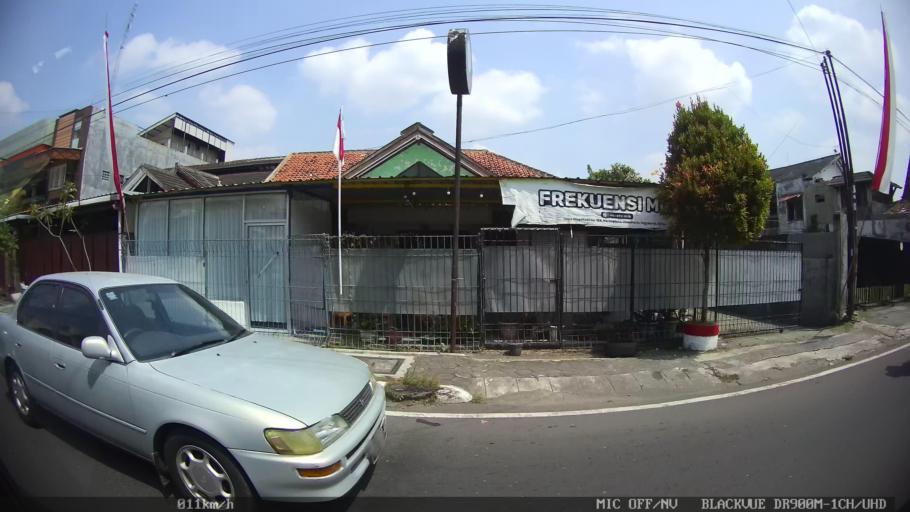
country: ID
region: Daerah Istimewa Yogyakarta
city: Yogyakarta
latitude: -7.8102
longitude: 110.3873
